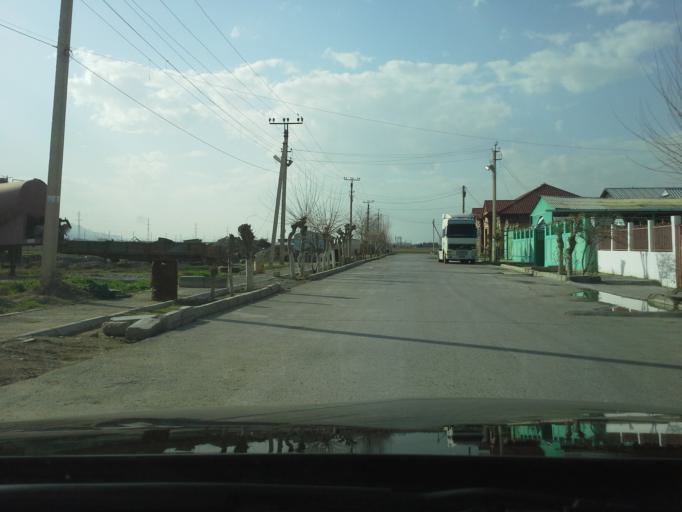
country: TM
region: Ahal
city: Abadan
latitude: 38.0158
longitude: 58.2299
